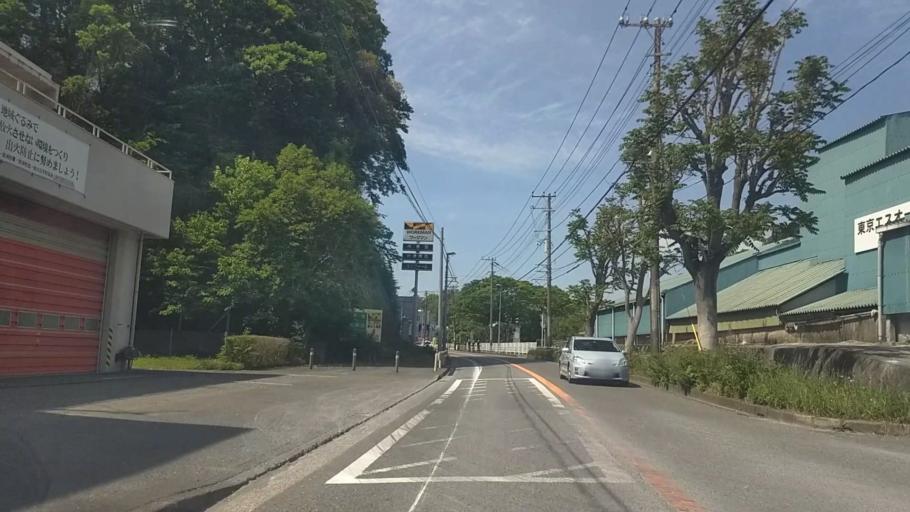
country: JP
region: Kanagawa
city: Kamakura
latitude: 35.3472
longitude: 139.5819
